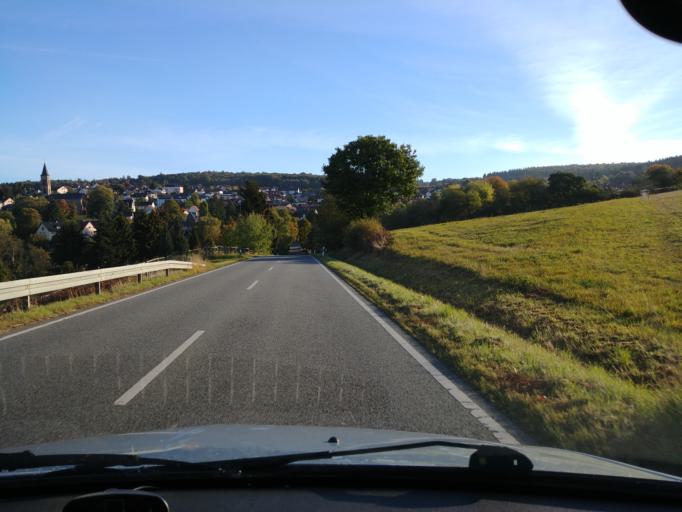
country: DE
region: Hesse
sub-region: Regierungsbezirk Darmstadt
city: Waldems
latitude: 50.2717
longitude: 8.3378
